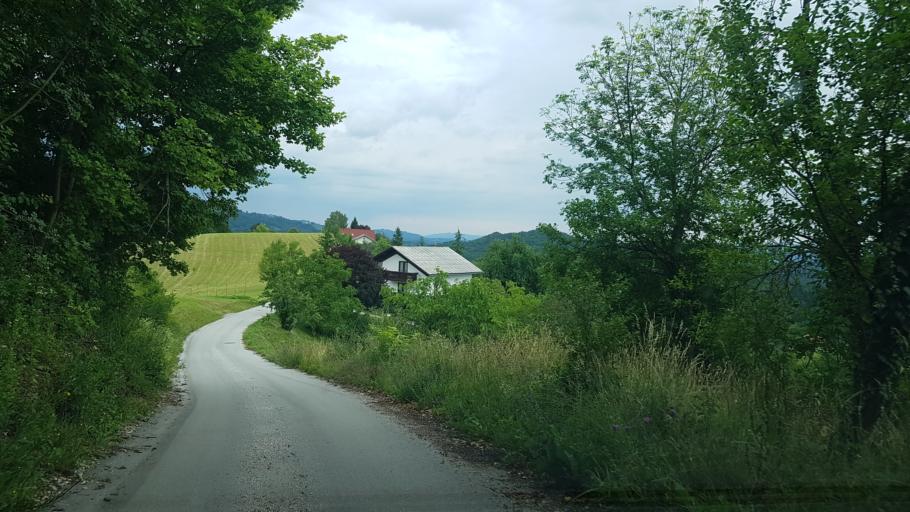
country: SI
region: Dobrna
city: Dobrna
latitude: 46.3475
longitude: 15.2492
